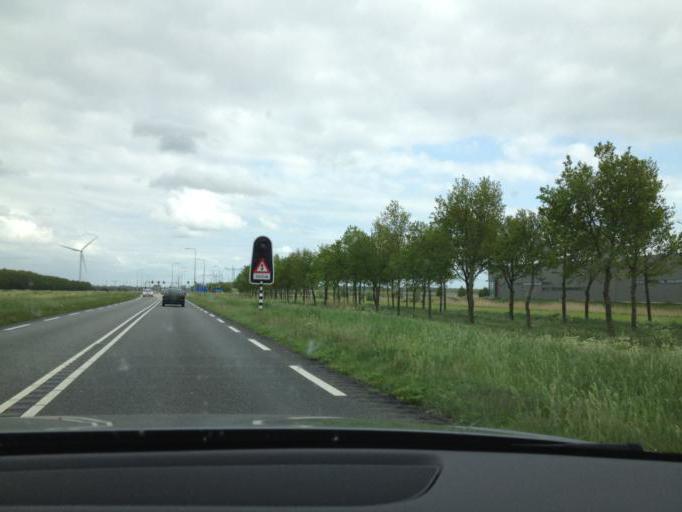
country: NL
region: North Holland
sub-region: Gemeente Huizen
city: Huizen
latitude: 52.3194
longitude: 5.3192
